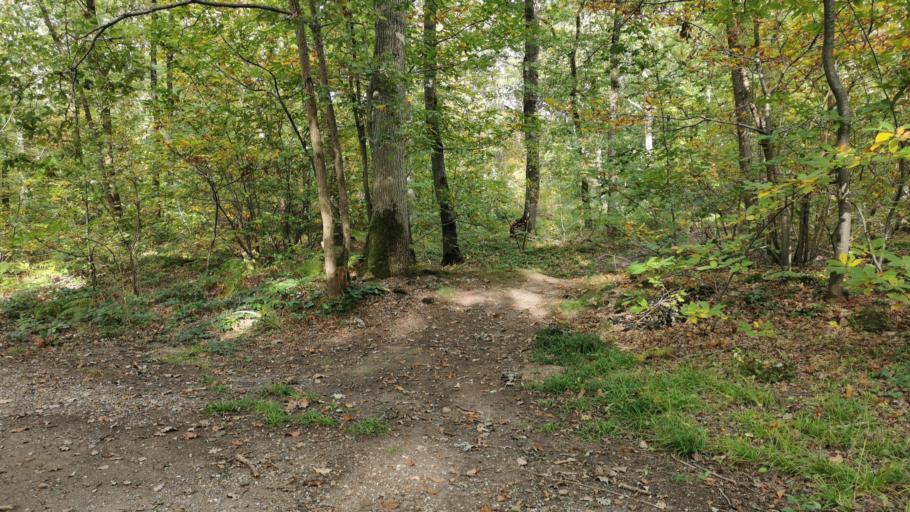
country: FR
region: Ile-de-France
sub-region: Departement des Yvelines
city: Neauphle-le-Chateau
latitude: 48.8019
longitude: 1.9207
